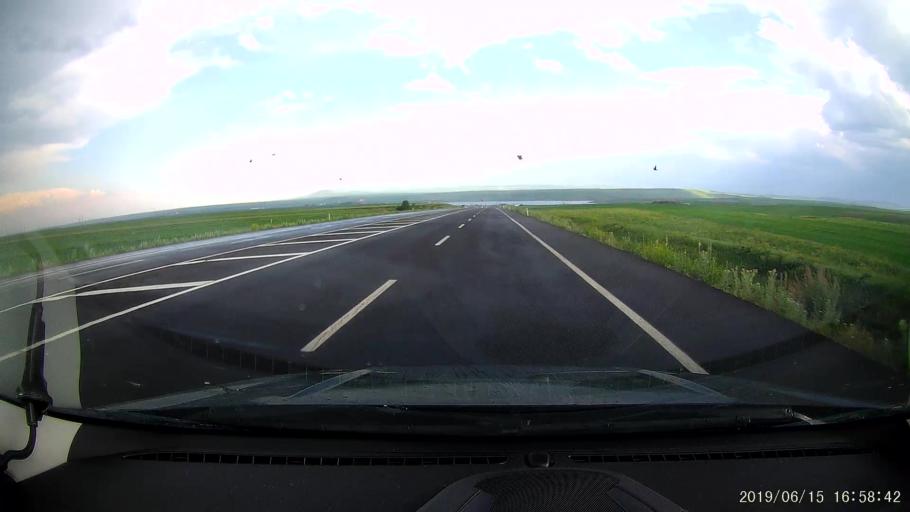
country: TR
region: Kars
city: Susuz
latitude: 40.7617
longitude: 43.1452
